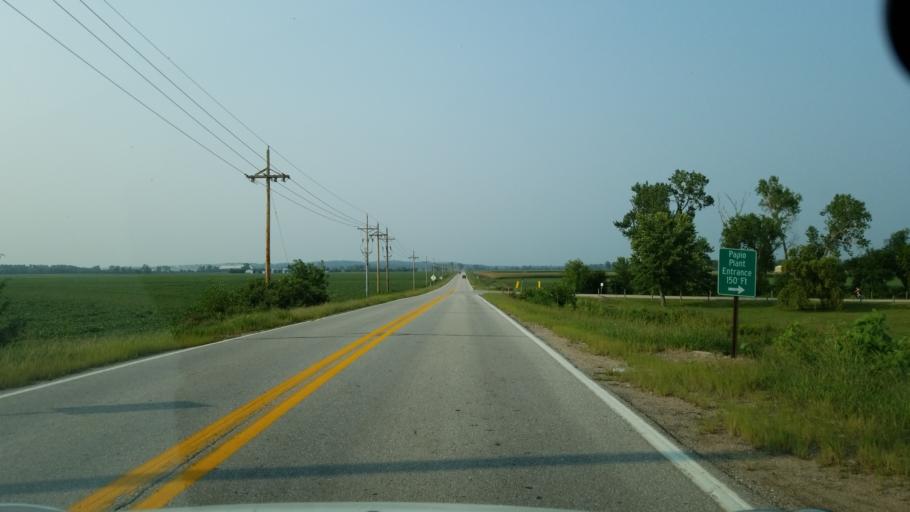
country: US
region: Nebraska
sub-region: Sarpy County
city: Offutt Air Force Base
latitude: 41.0822
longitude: -95.8898
